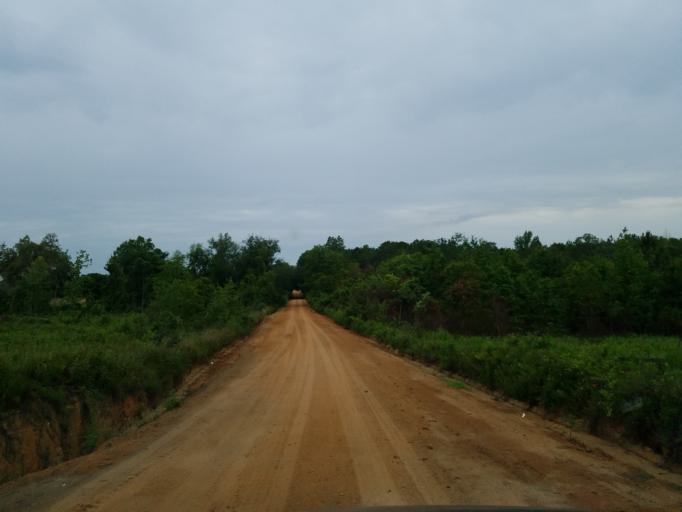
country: US
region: Georgia
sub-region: Crisp County
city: Cordele
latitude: 32.0023
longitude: -83.6974
